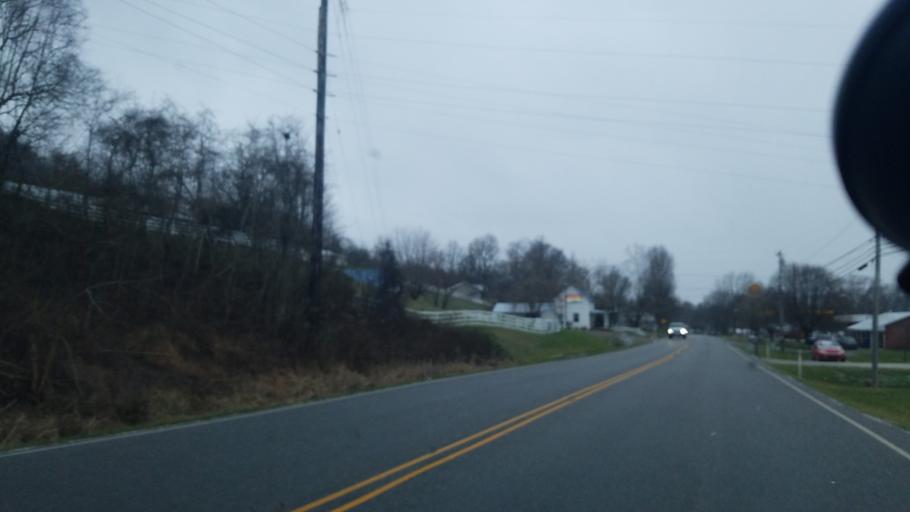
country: US
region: Ohio
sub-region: Scioto County
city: Portsmouth
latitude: 38.7198
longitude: -83.0180
